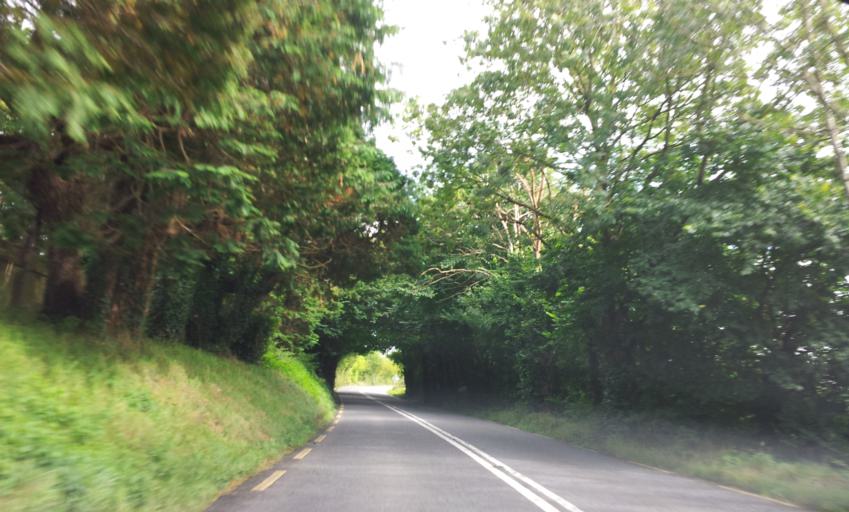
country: IE
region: Munster
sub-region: Ciarrai
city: Killorglin
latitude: 52.1011
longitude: -9.7161
